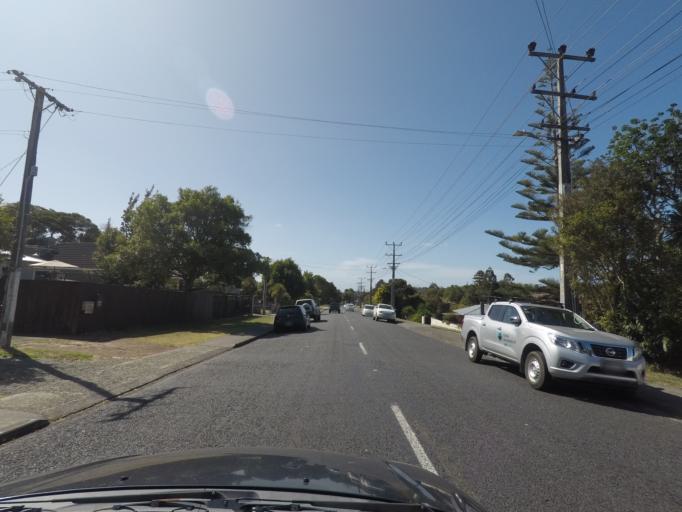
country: NZ
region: Auckland
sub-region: Auckland
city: Titirangi
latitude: -36.9302
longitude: 174.6551
